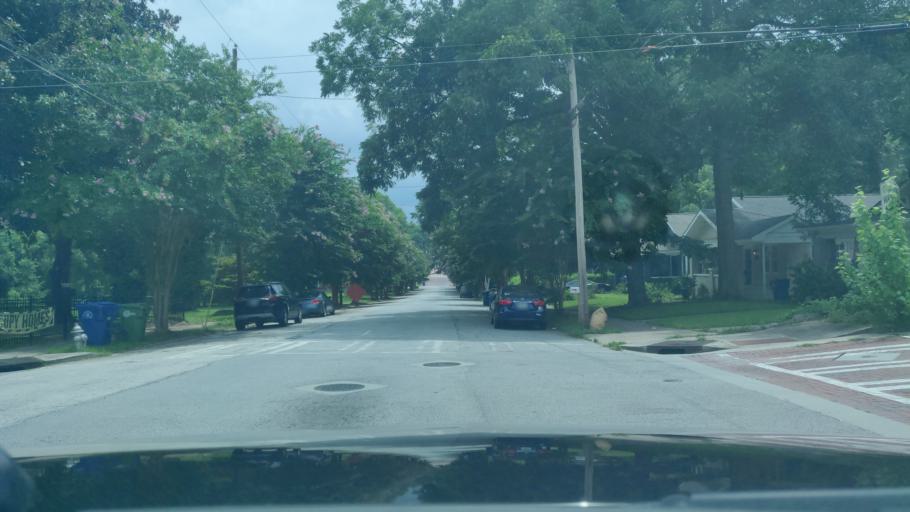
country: US
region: Georgia
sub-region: Fulton County
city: Atlanta
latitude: 33.7303
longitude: -84.3834
